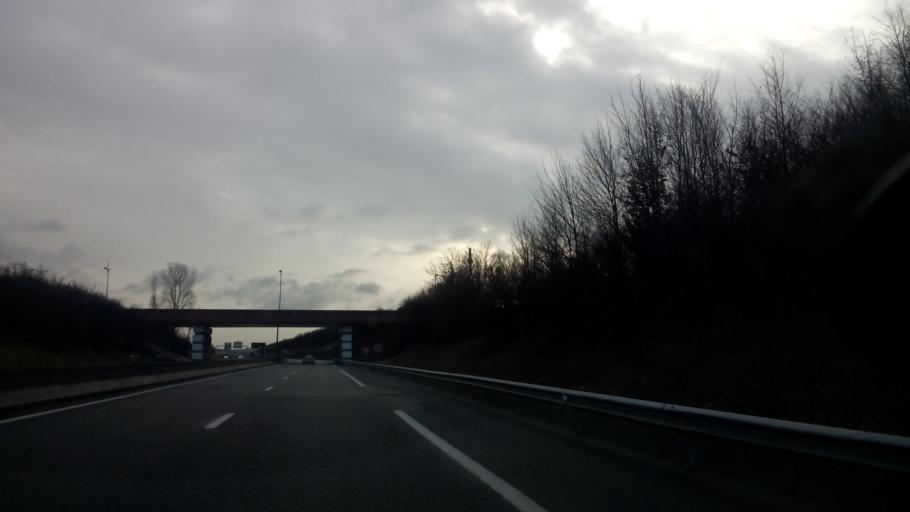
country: FR
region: Rhone-Alpes
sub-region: Departement du Rhone
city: Corbas
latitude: 45.6779
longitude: 4.8991
